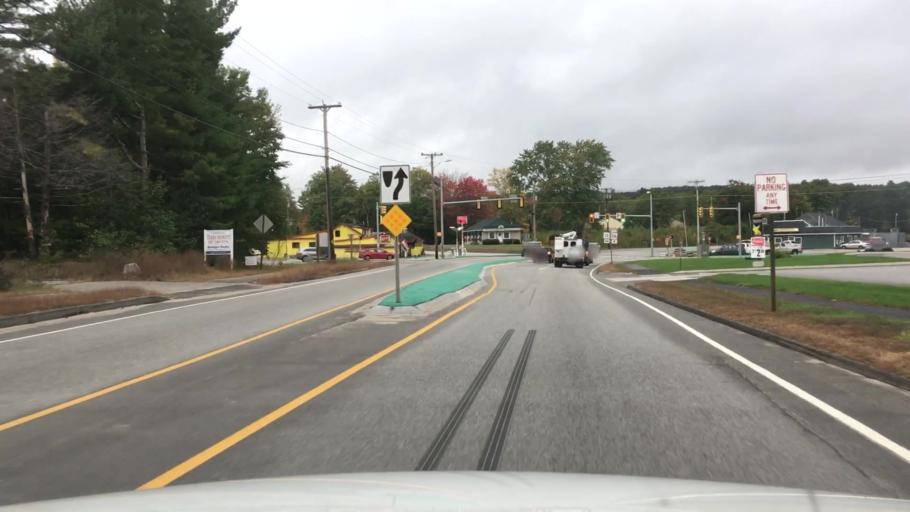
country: US
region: Maine
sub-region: Androscoggin County
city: Poland
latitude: 44.0746
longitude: -70.4154
